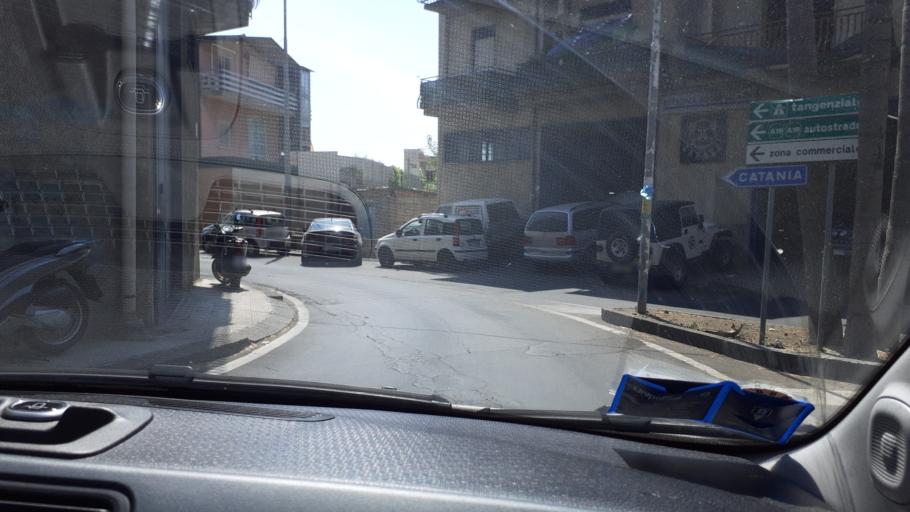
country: IT
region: Sicily
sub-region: Catania
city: Misterbianco
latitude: 37.5176
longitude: 15.0161
